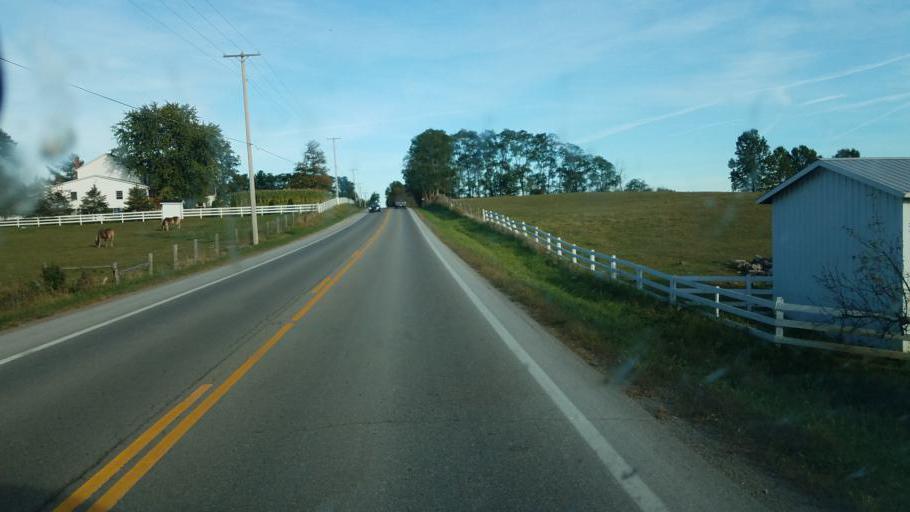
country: US
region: Ohio
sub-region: Ashland County
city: Ashland
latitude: 40.8862
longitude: -82.3990
